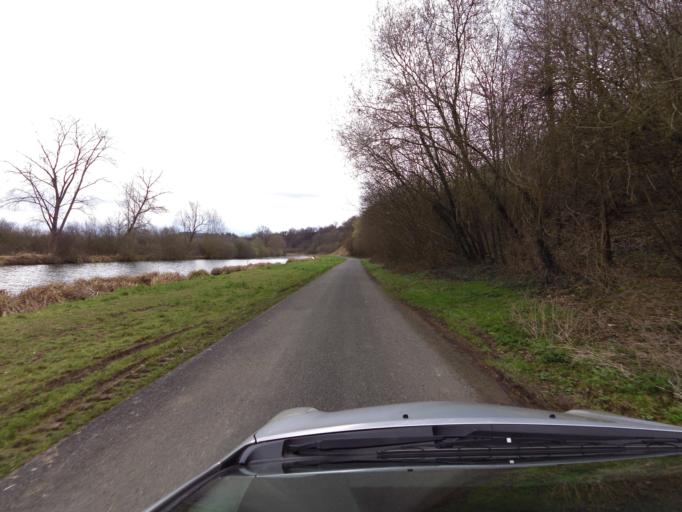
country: FR
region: Picardie
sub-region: Departement de la Somme
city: Bray-sur-Somme
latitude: 49.9320
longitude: 2.8019
